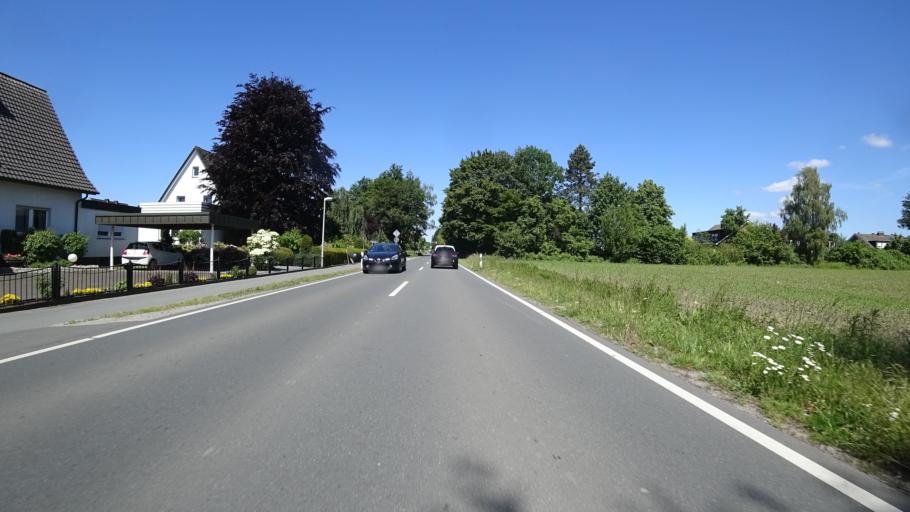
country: DE
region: North Rhine-Westphalia
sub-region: Regierungsbezirk Detmold
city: Guetersloh
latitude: 51.9012
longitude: 8.4399
